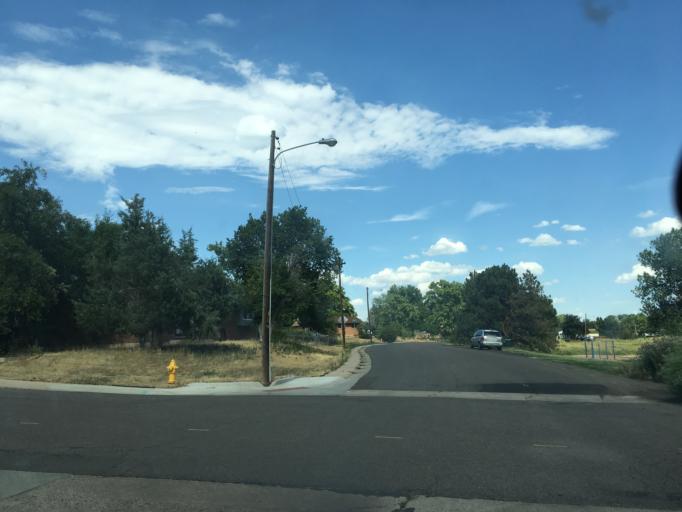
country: US
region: Colorado
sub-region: Jefferson County
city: Lakewood
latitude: 39.6855
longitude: -105.0434
